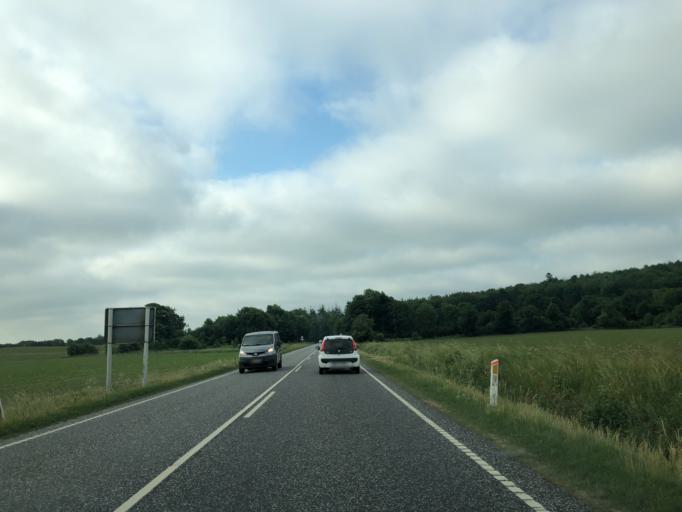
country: DK
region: South Denmark
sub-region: Vejle Kommune
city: Give
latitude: 55.7677
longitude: 9.2904
